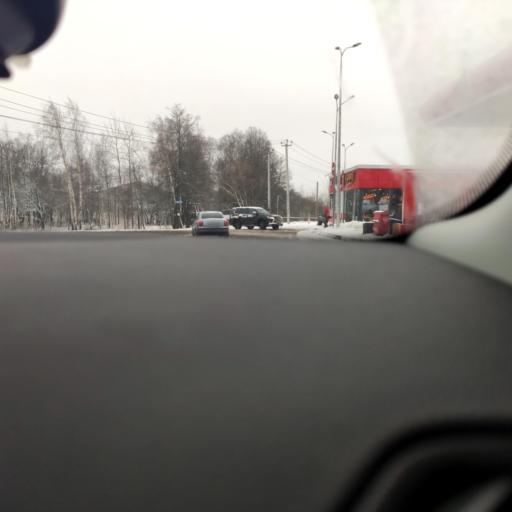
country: RU
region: Moskovskaya
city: Shcherbinka
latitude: 55.4686
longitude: 37.5964
